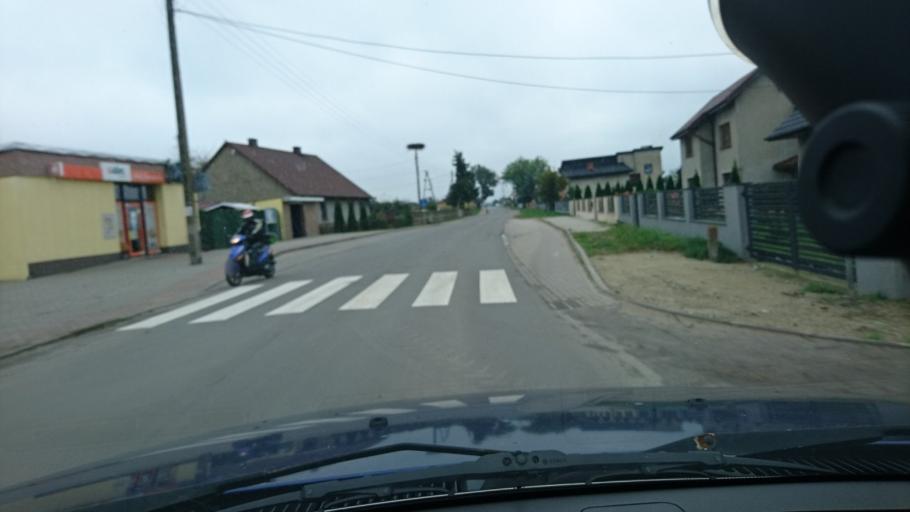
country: PL
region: Greater Poland Voivodeship
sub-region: Powiat ostrowski
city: Odolanow
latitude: 51.5744
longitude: 17.6307
